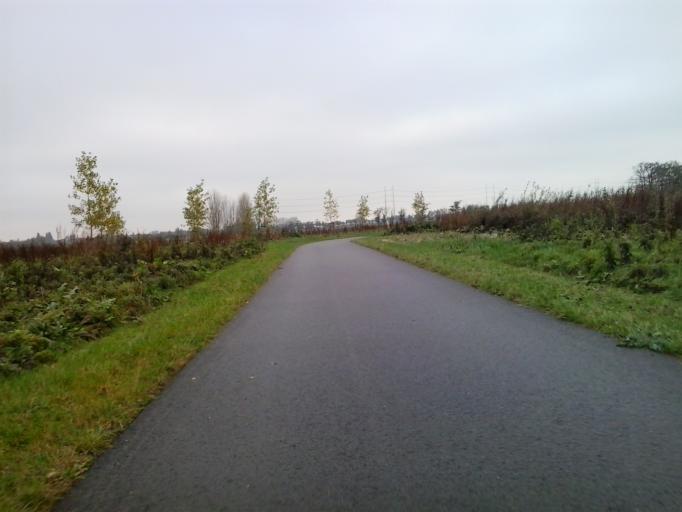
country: NL
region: South Holland
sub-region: Gemeente Lansingerland
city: Berkel en Rodenrijs
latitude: 52.0075
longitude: 4.4669
